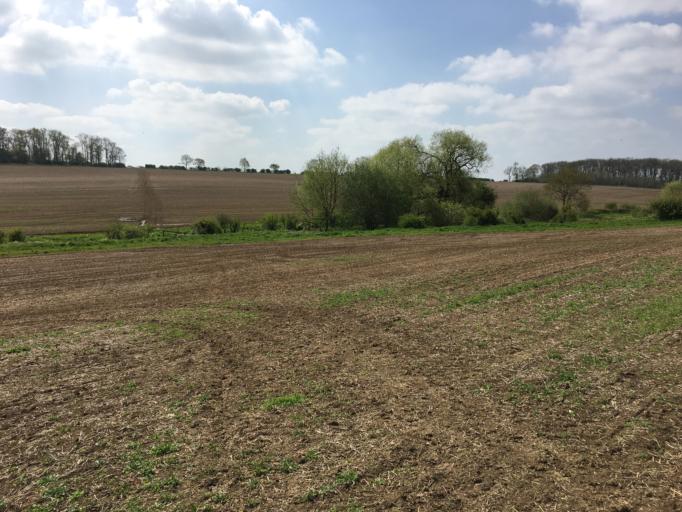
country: GB
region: England
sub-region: Leicestershire
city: Houghton on the Hill
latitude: 52.6131
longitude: -0.9955
